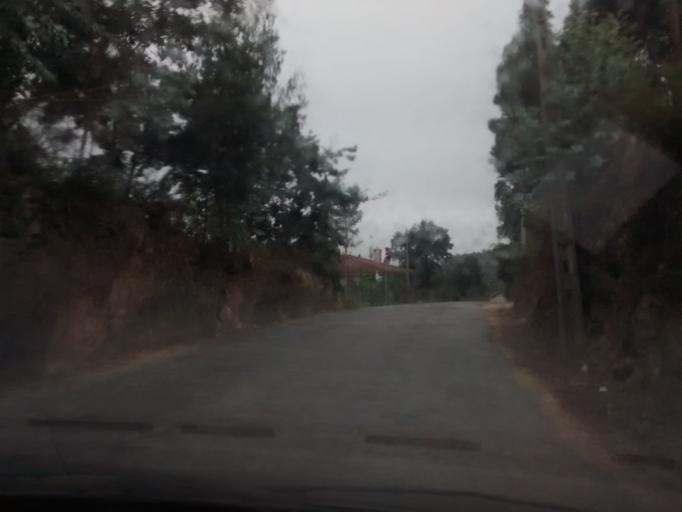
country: PT
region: Braga
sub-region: Braga
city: Oliveira
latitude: 41.4589
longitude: -8.5155
